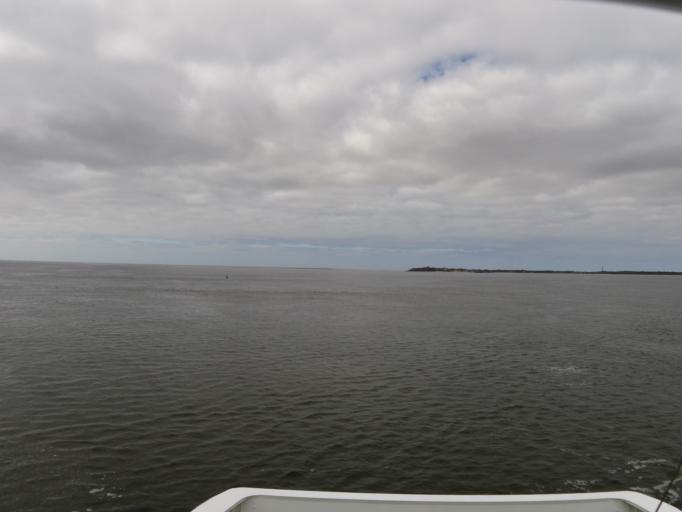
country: DE
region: Schleswig-Holstein
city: Wittdun
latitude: 54.6366
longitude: 8.4346
